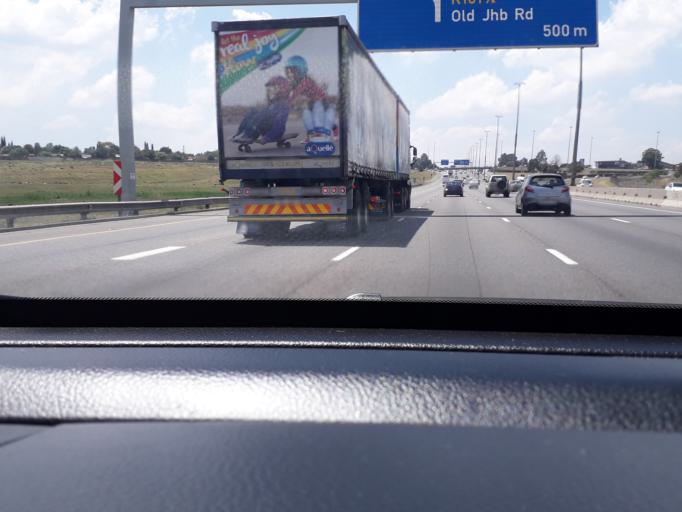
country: ZA
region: Gauteng
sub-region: City of Tshwane Metropolitan Municipality
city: Centurion
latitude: -25.9140
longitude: 28.1542
